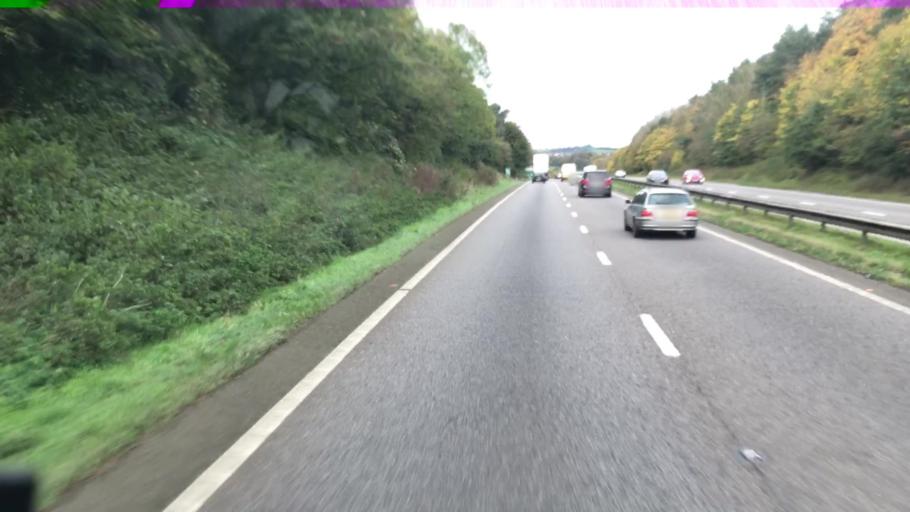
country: GB
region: England
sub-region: Devon
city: Exeter
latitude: 50.6933
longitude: -3.5395
